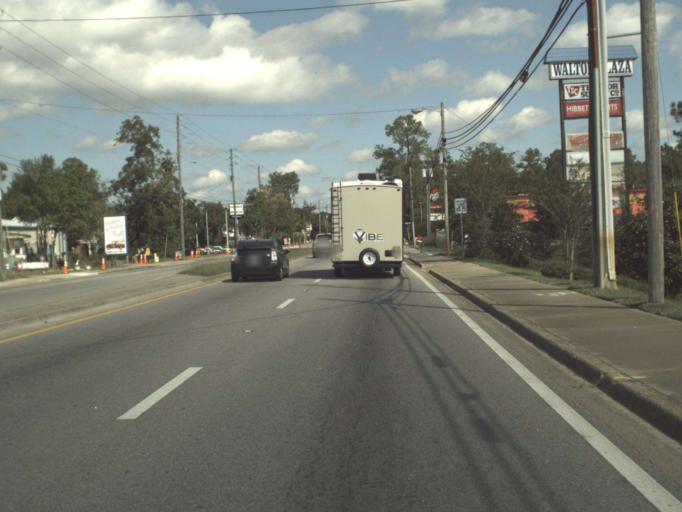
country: US
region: Florida
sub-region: Walton County
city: DeFuniak Springs
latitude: 30.7080
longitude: -86.1227
